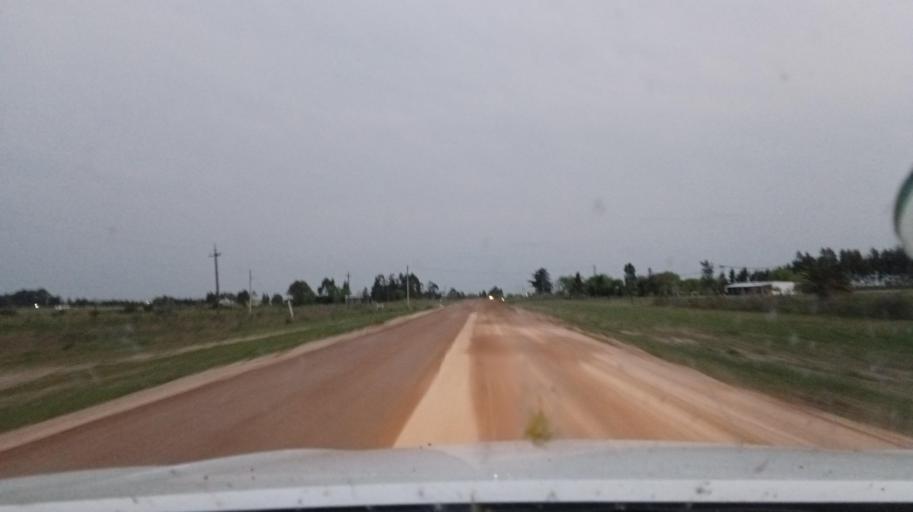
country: UY
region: Canelones
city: Santa Rosa
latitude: -34.5407
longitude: -56.1001
